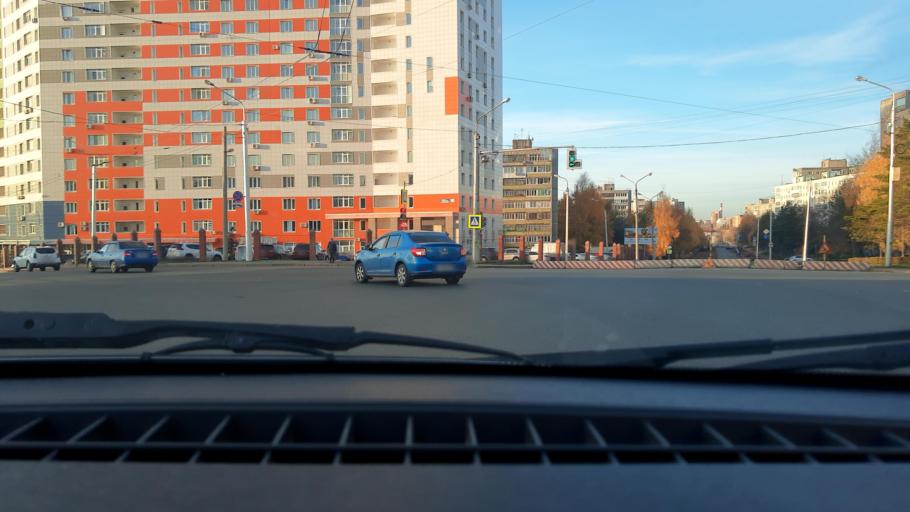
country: RU
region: Bashkortostan
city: Ufa
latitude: 54.7627
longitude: 56.0225
